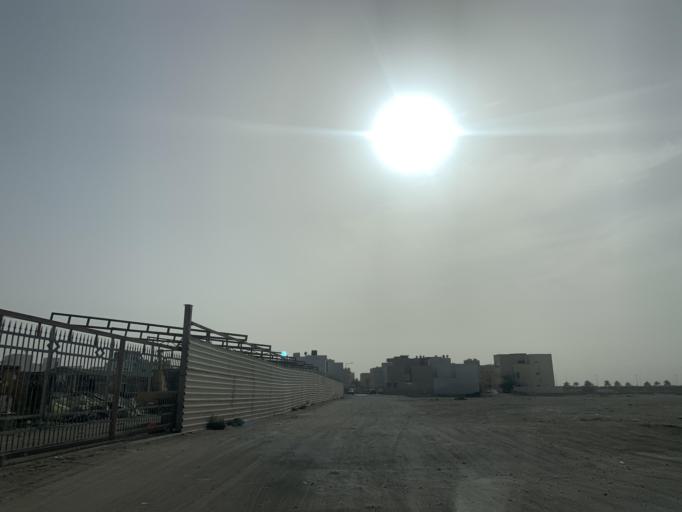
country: BH
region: Northern
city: Madinat `Isa
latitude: 26.1593
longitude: 50.5107
